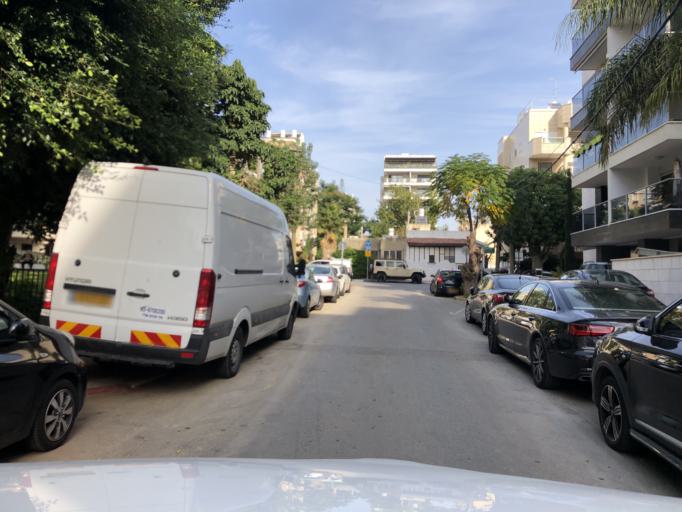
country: IL
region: Tel Aviv
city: Bene Beraq
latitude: 32.0719
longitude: 34.8263
